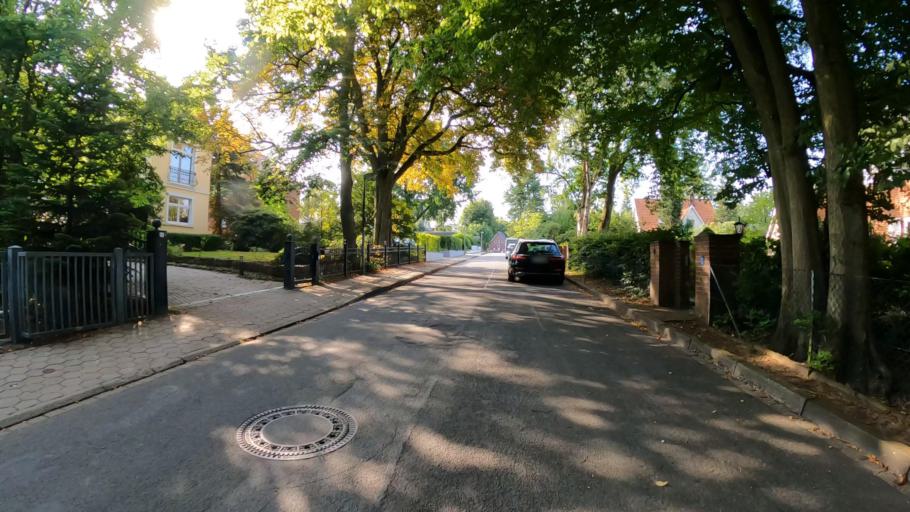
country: DE
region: Schleswig-Holstein
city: Wentorf bei Hamburg
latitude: 53.4986
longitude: 10.2504
